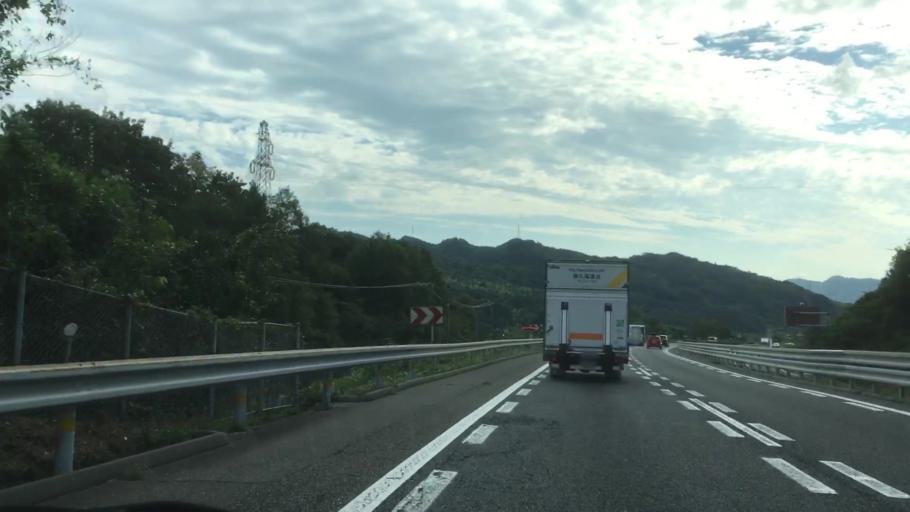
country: JP
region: Yamaguchi
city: Iwakuni
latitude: 34.1072
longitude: 132.1135
